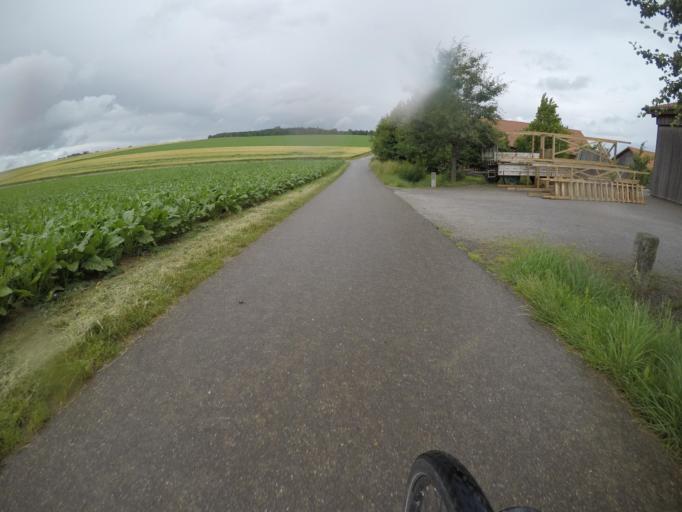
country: DE
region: Baden-Wuerttemberg
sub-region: Regierungsbezirk Stuttgart
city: Bondorf
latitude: 48.5592
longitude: 8.8284
